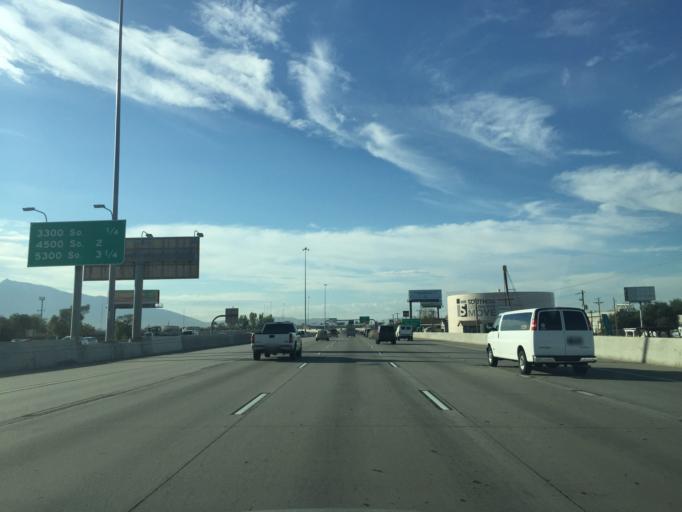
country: US
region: Utah
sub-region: Salt Lake County
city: Centerfield
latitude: 40.7080
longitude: -111.9040
